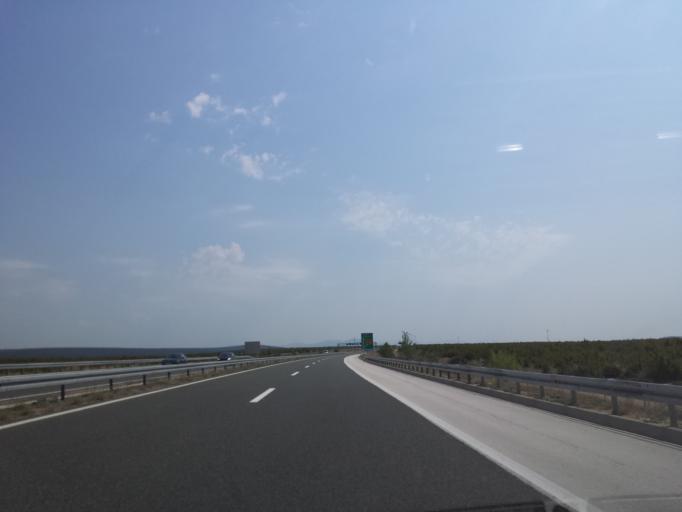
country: HR
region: Sibensko-Kniniska
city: Zaton
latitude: 43.8979
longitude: 15.7797
